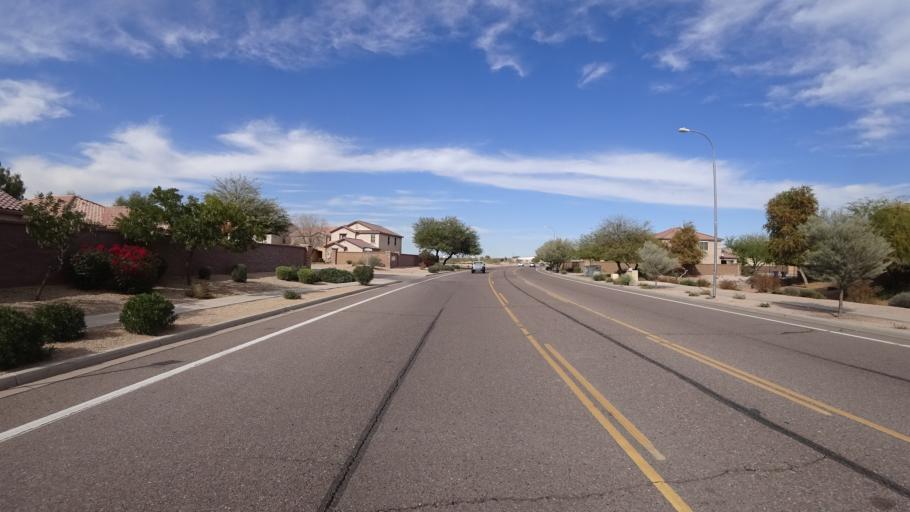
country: US
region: Arizona
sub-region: Maricopa County
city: Tolleson
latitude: 33.4698
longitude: -112.2648
